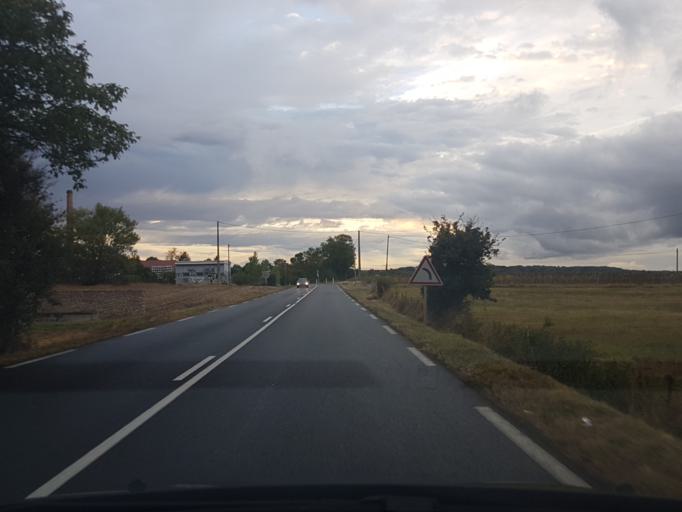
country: FR
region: Midi-Pyrenees
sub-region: Departement de l'Ariege
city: La Tour-du-Crieu
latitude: 43.0896
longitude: 1.7331
